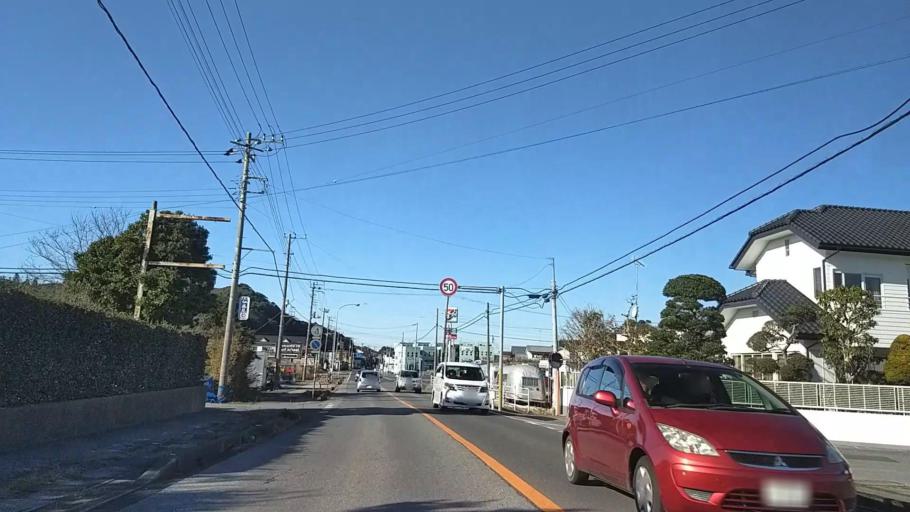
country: JP
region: Chiba
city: Ohara
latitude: 35.3245
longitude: 140.4010
